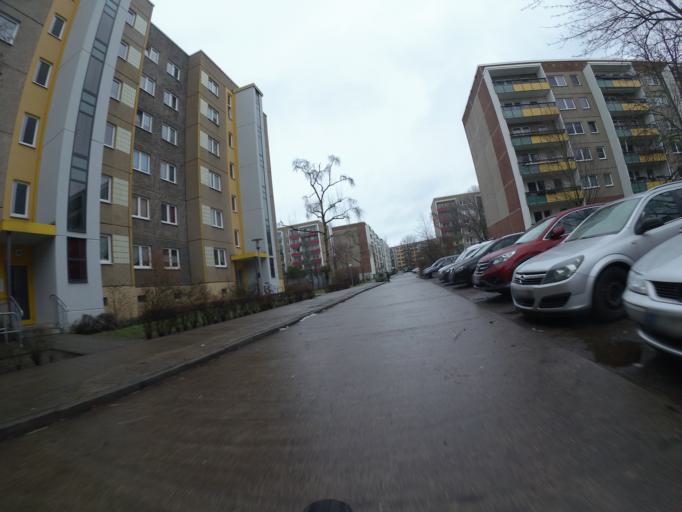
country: DE
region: Berlin
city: Marzahn
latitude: 52.5501
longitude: 13.5806
